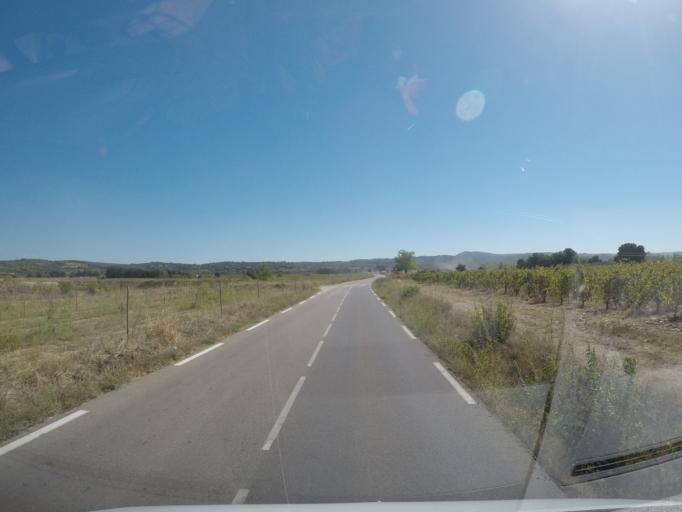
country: FR
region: Languedoc-Roussillon
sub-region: Departement de l'Herault
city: Saint-Jean-de-Fos
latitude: 43.7016
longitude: 3.5676
